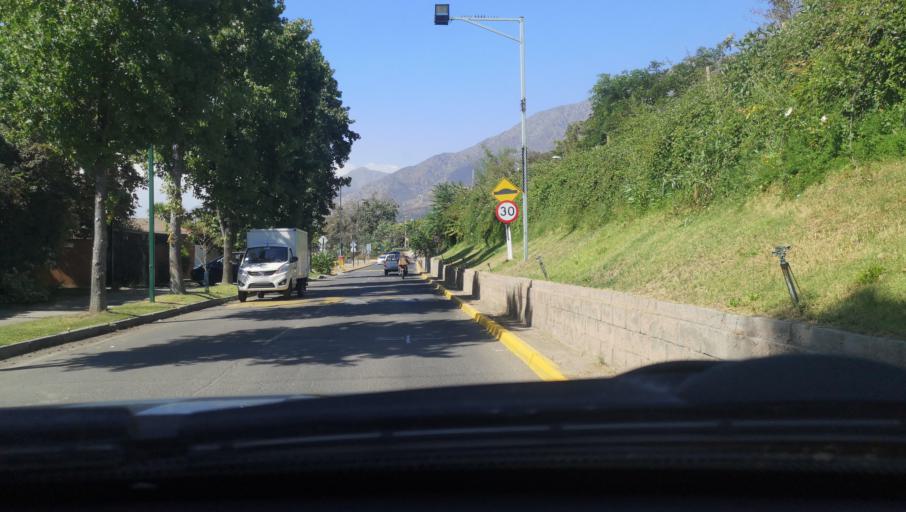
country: CL
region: Santiago Metropolitan
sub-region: Provincia de Santiago
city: Villa Presidente Frei, Nunoa, Santiago, Chile
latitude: -33.4841
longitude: -70.5373
